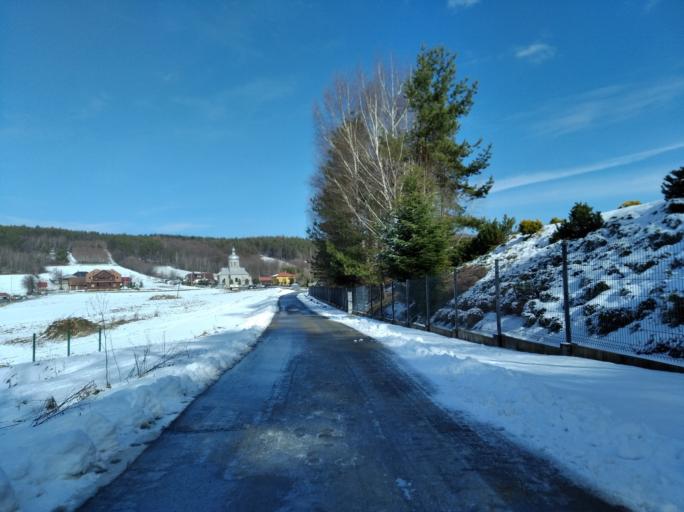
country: PL
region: Subcarpathian Voivodeship
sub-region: Powiat krosnienski
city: Korczyna
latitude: 49.7448
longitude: 21.8178
